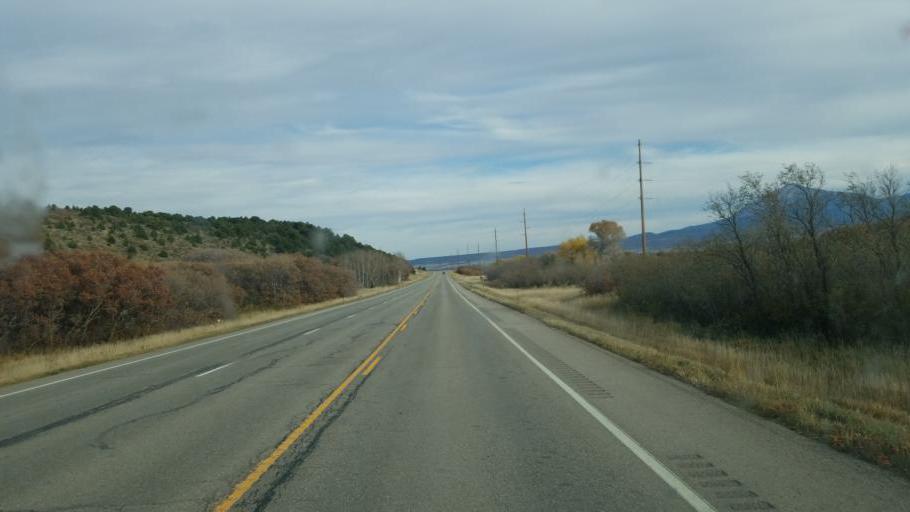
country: US
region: Colorado
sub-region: Huerfano County
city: Walsenburg
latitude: 37.5487
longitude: -105.0961
